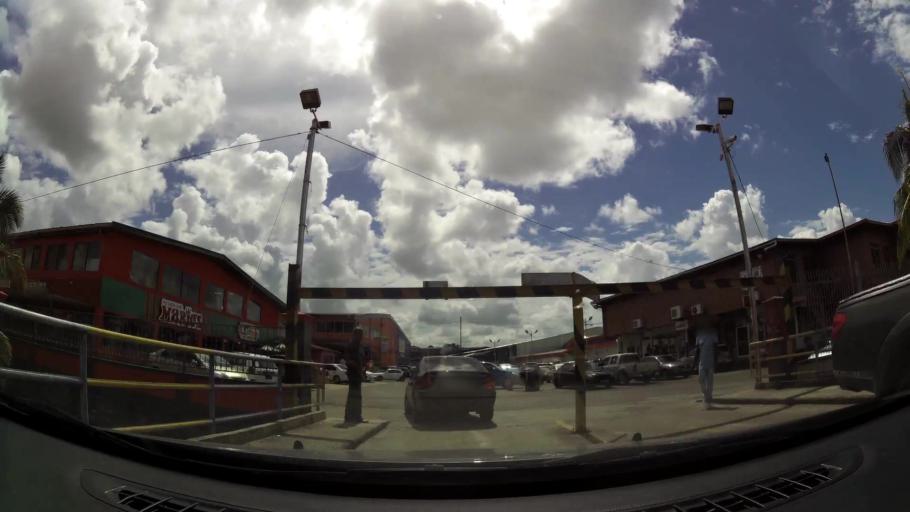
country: TT
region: City of San Fernando
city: Marabella
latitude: 10.3020
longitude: -61.4478
